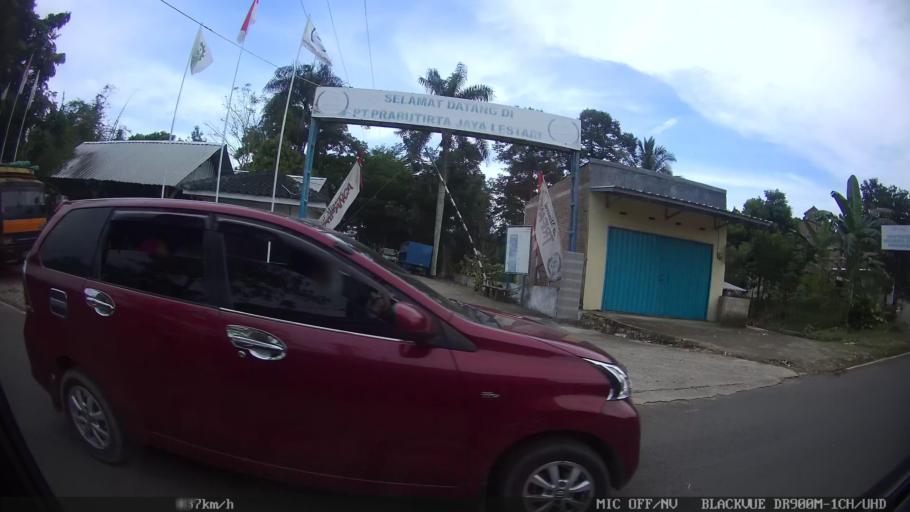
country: ID
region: Lampung
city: Bandarlampung
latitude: -5.4306
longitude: 105.2044
